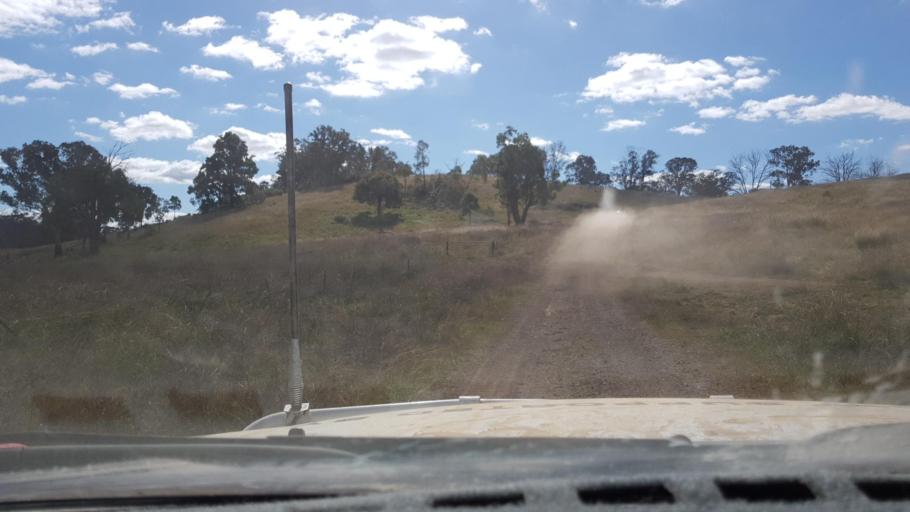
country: AU
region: New South Wales
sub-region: Tamworth Municipality
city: Manilla
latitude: -30.4402
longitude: 150.8378
